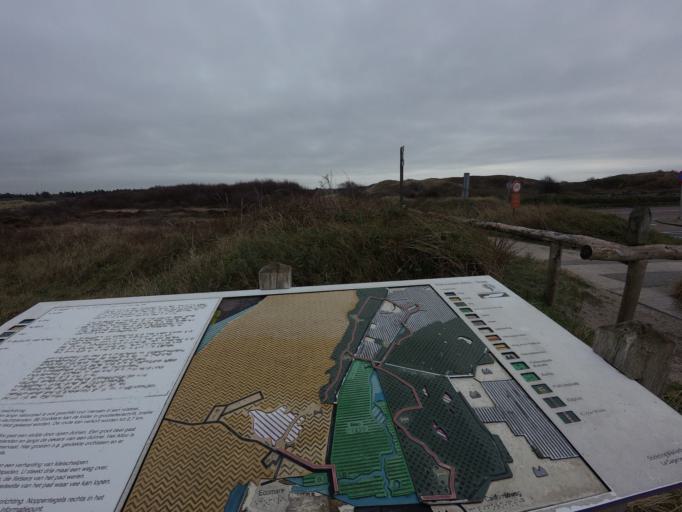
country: NL
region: North Holland
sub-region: Gemeente Texel
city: Den Burg
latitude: 53.0792
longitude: 4.7457
